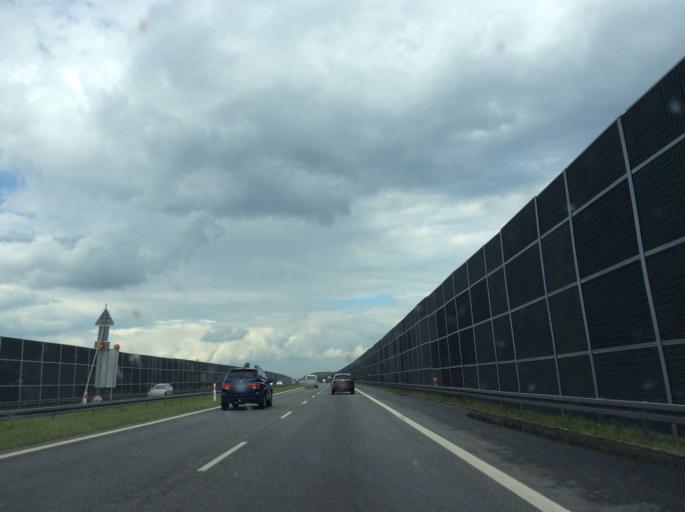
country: PL
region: Masovian Voivodeship
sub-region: Powiat pruszkowski
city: Brwinow
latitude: 52.1667
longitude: 20.7408
